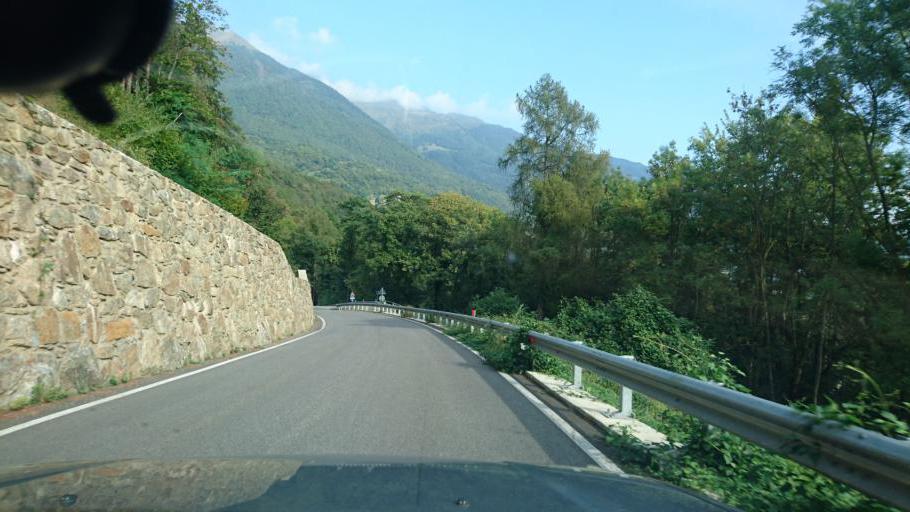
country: IT
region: Lombardy
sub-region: Provincia di Brescia
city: Paisco Loveno
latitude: 46.0985
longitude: 10.3082
